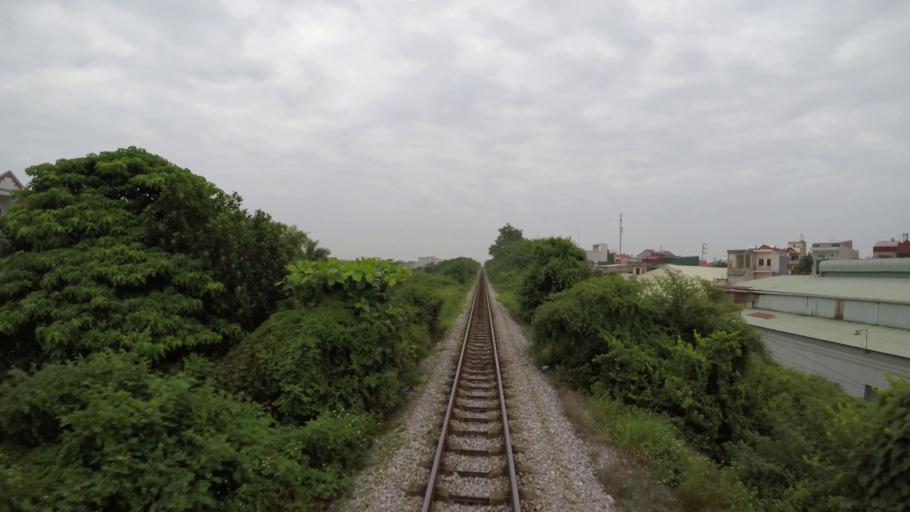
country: VN
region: Hai Duong
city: Thanh Pho Hai Duong
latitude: 20.9501
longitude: 106.3620
